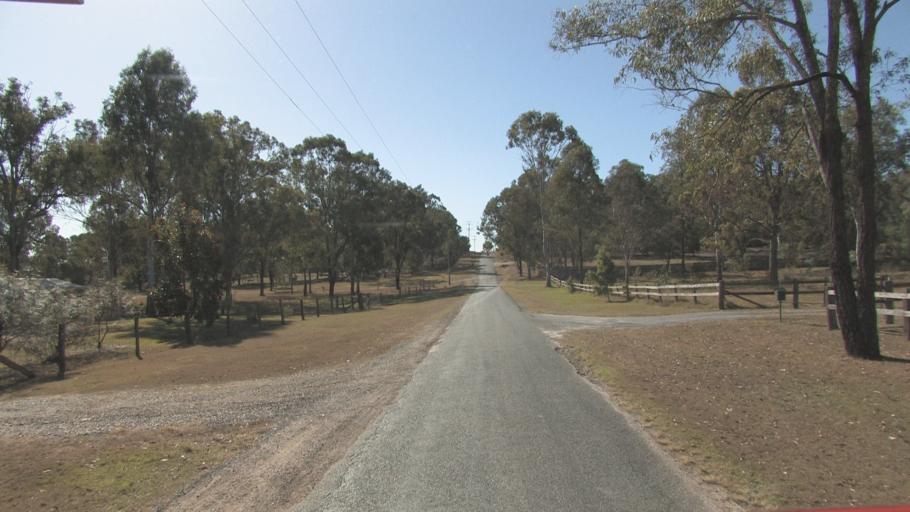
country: AU
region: Queensland
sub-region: Logan
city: Cedar Vale
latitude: -27.8631
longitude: 153.0264
